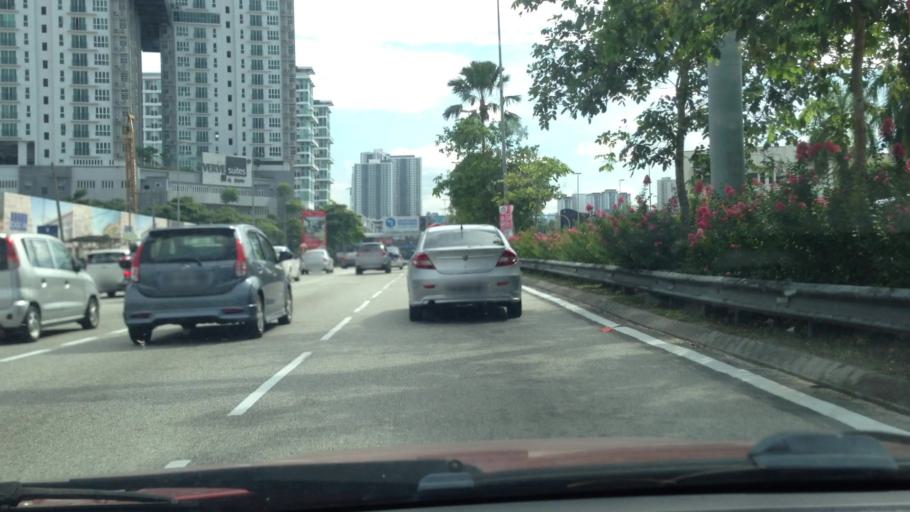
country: MY
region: Kuala Lumpur
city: Kuala Lumpur
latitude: 3.0901
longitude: 101.6744
